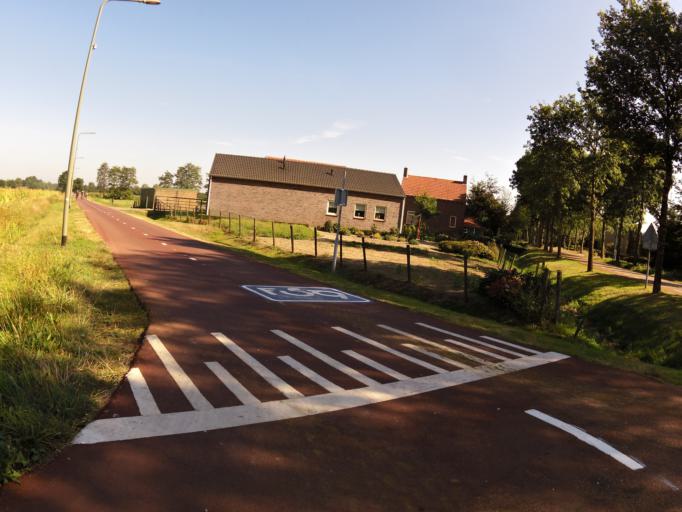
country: NL
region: North Brabant
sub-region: Gemeente Maasdonk
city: Geffen
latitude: 51.7483
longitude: 5.4802
